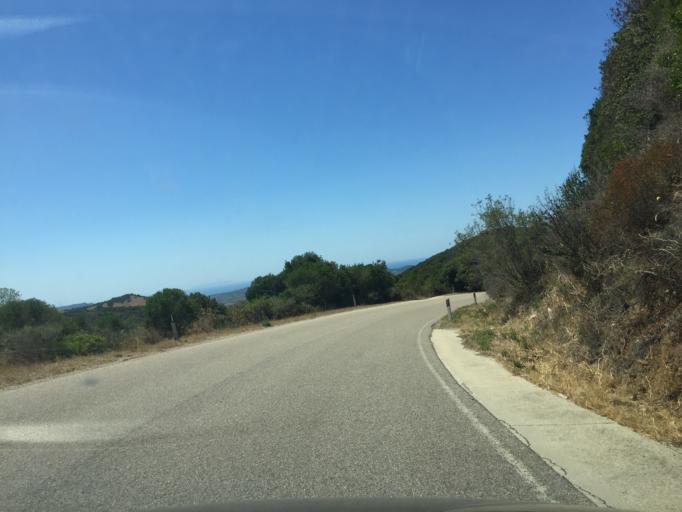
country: IT
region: Sardinia
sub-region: Provincia di Olbia-Tempio
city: Aglientu
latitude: 41.0873
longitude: 9.1086
